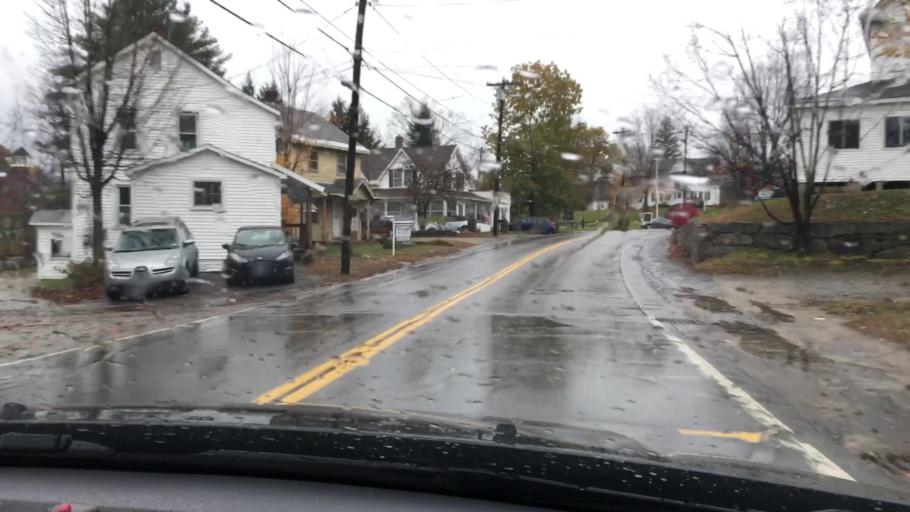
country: US
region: New Hampshire
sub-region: Grafton County
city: Ashland
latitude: 43.6964
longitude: -71.6307
